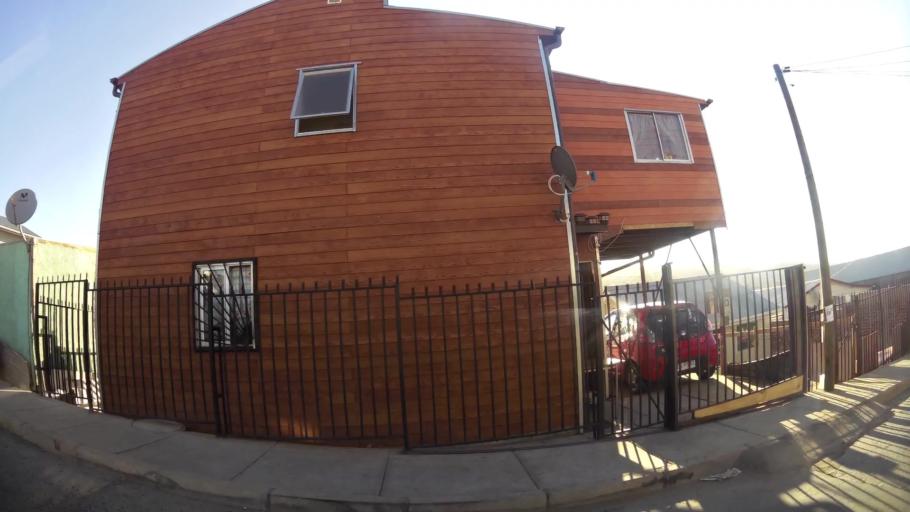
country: CL
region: Valparaiso
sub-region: Provincia de Valparaiso
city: Valparaiso
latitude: -33.0609
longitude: -71.6125
